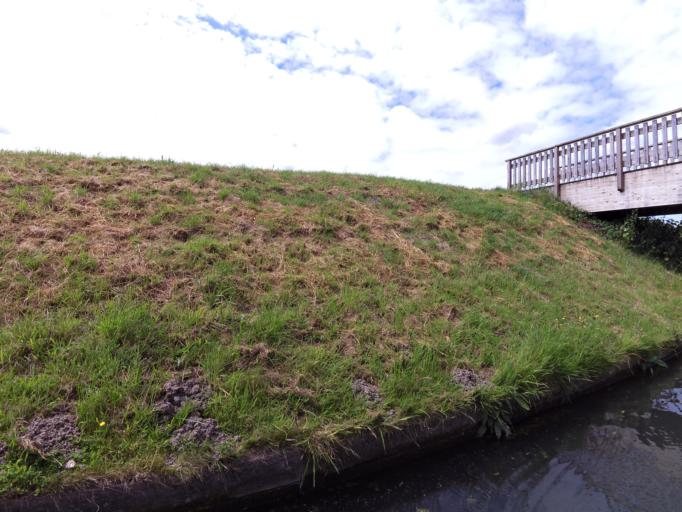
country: FR
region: Nord-Pas-de-Calais
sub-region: Departement du Pas-de-Calais
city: Saint-Omer
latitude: 50.7578
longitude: 2.2468
